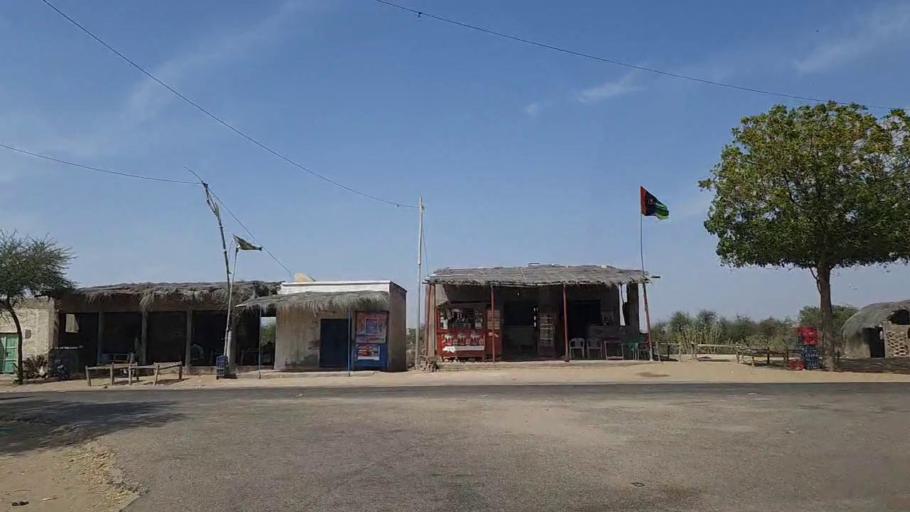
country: PK
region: Sindh
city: Umarkot
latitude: 25.1626
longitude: 70.0060
